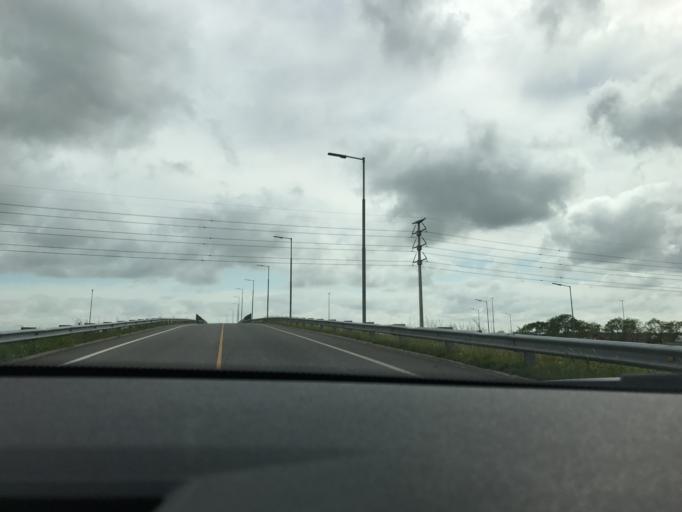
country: AR
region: Buenos Aires
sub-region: Partido de La Plata
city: La Plata
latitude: -34.8401
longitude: -58.0712
